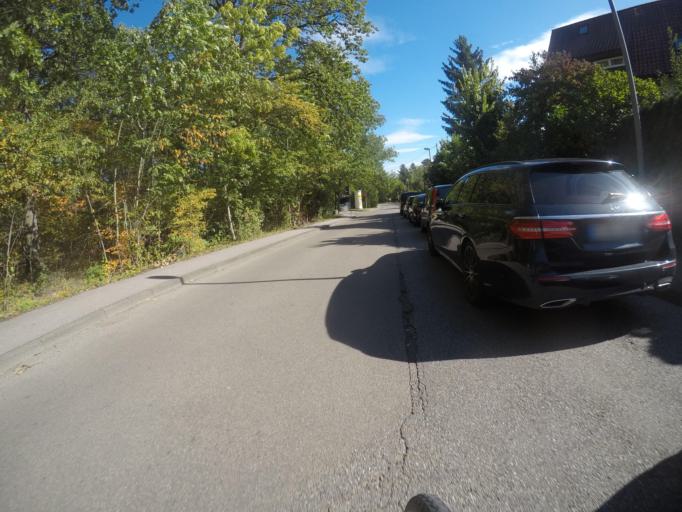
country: DE
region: Baden-Wuerttemberg
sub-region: Regierungsbezirk Stuttgart
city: Stuttgart-Ost
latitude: 48.7613
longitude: 9.2250
